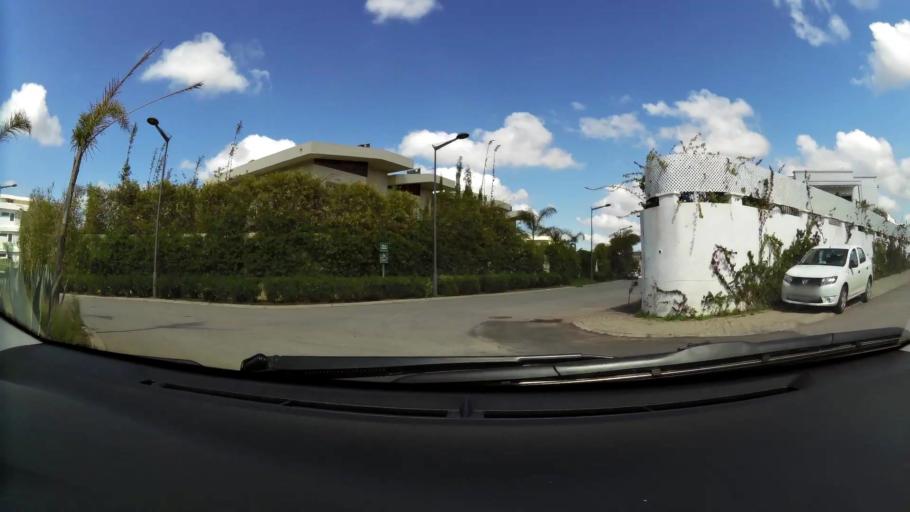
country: MA
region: Grand Casablanca
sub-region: Nouaceur
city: Bouskoura
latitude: 33.4674
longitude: -7.6071
